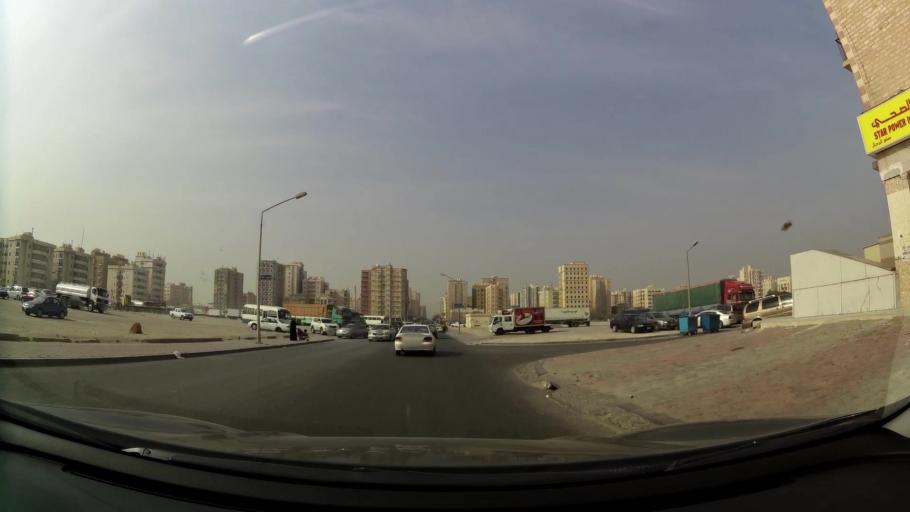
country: KW
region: Al Farwaniyah
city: Al Farwaniyah
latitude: 29.2707
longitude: 47.9582
